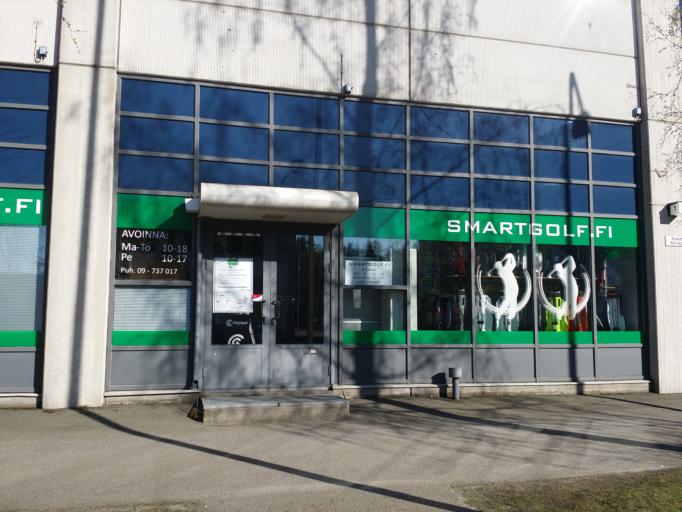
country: FI
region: Uusimaa
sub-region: Helsinki
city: Vantaa
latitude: 60.2098
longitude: 25.0540
